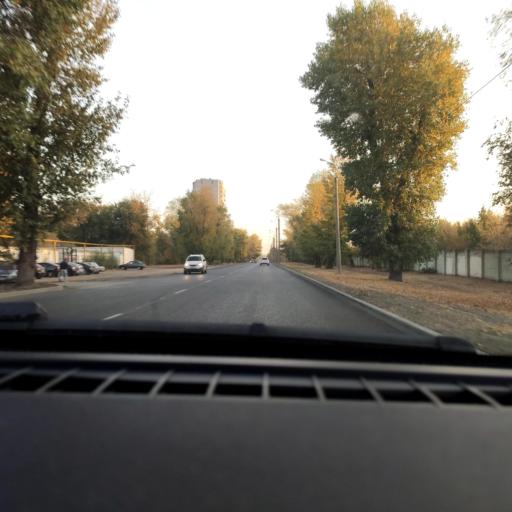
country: RU
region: Voronezj
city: Voronezh
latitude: 51.6513
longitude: 39.2457
